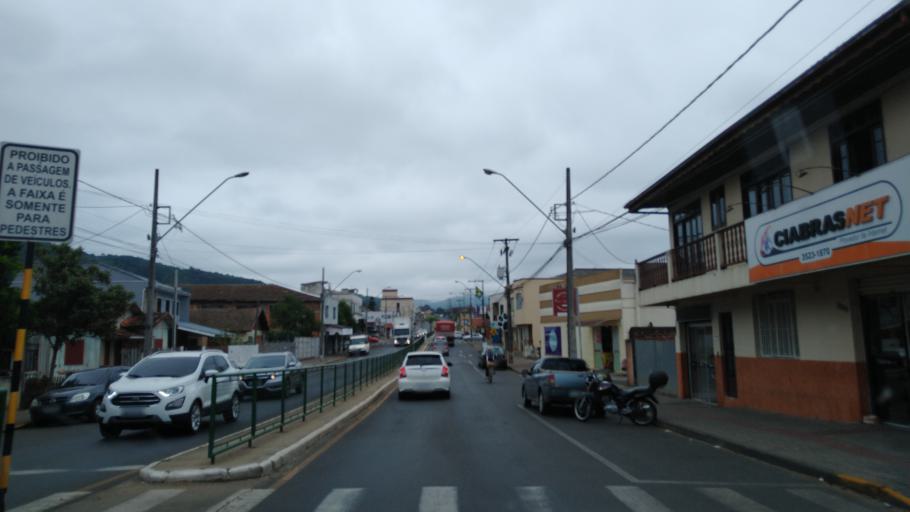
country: BR
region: Santa Catarina
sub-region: Porto Uniao
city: Porto Uniao
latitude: -26.2513
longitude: -51.0853
